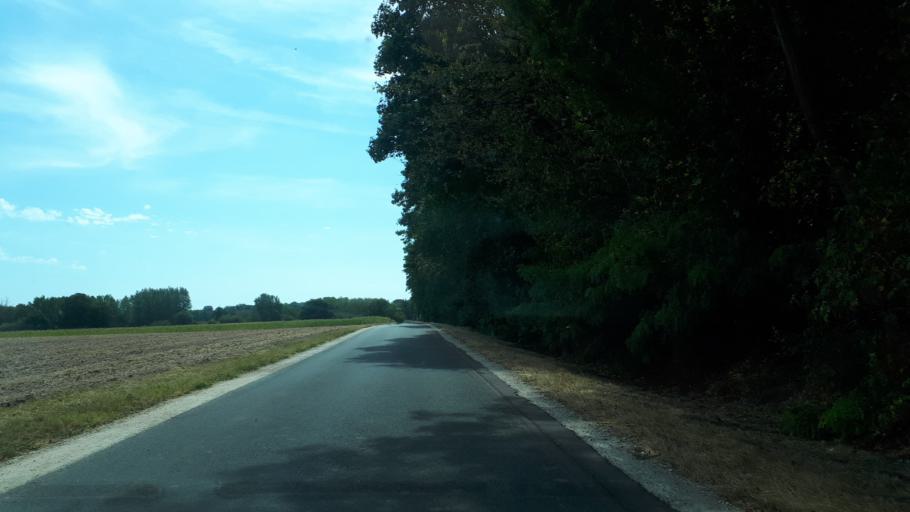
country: FR
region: Centre
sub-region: Departement du Loir-et-Cher
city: Chitenay
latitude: 47.4425
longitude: 1.3498
